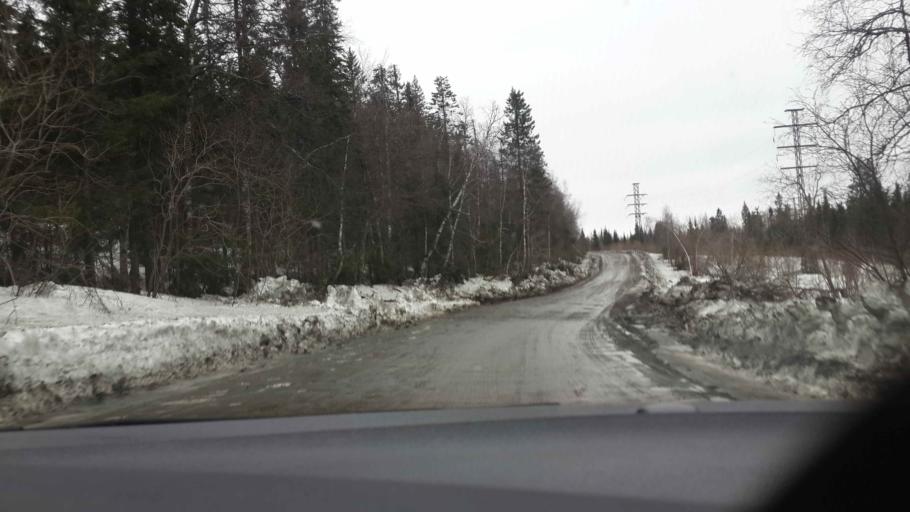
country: RU
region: Chelyabinsk
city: Magnitka
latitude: 55.2662
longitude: 59.6996
